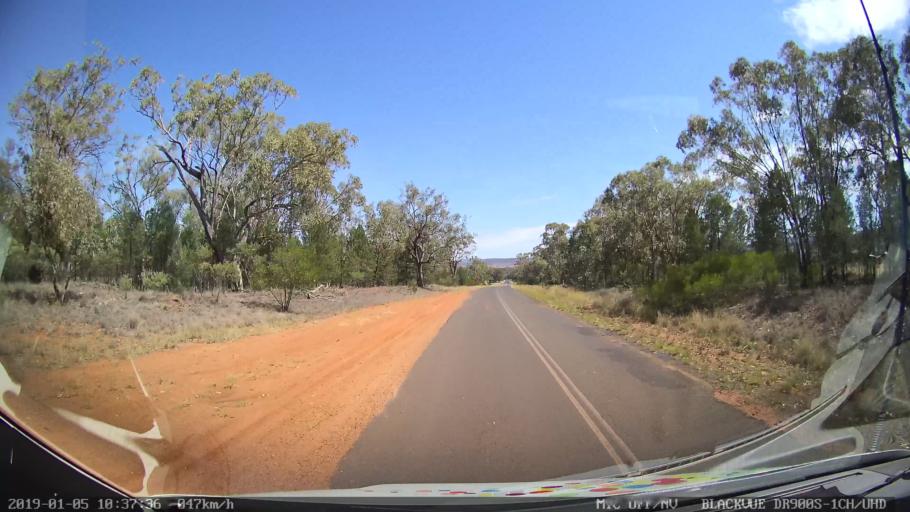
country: AU
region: New South Wales
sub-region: Gilgandra
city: Gilgandra
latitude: -31.4735
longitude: 148.9211
